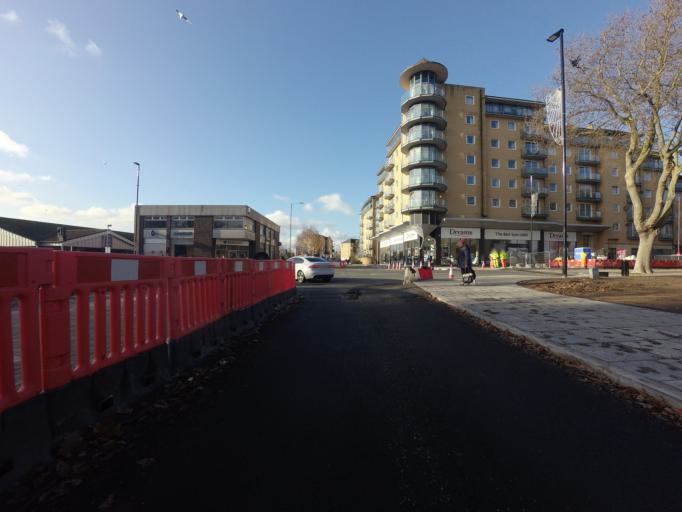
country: GB
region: England
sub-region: Greater London
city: Feltham
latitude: 51.4440
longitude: -0.4109
